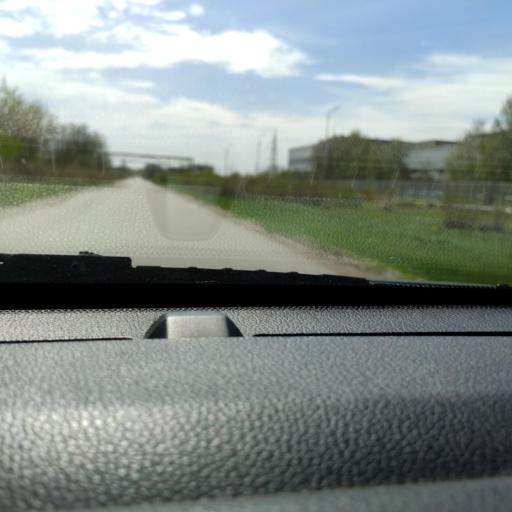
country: RU
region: Samara
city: Tol'yatti
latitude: 53.5815
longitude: 49.2383
